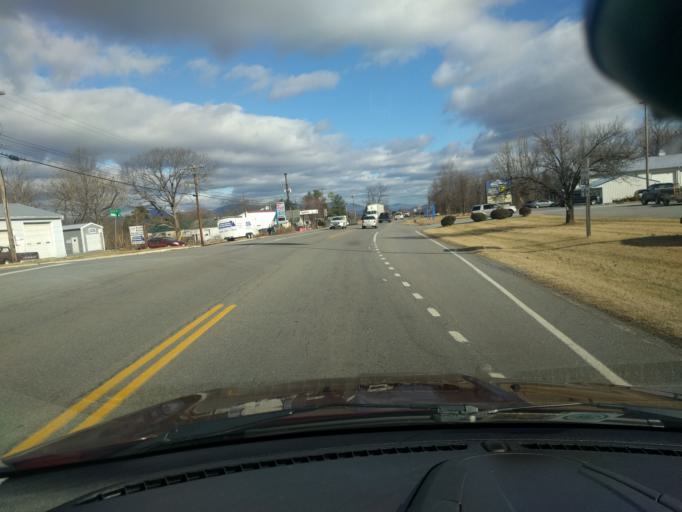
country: US
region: Virginia
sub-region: City of Bedford
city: Bedford
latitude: 37.3145
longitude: -79.5382
